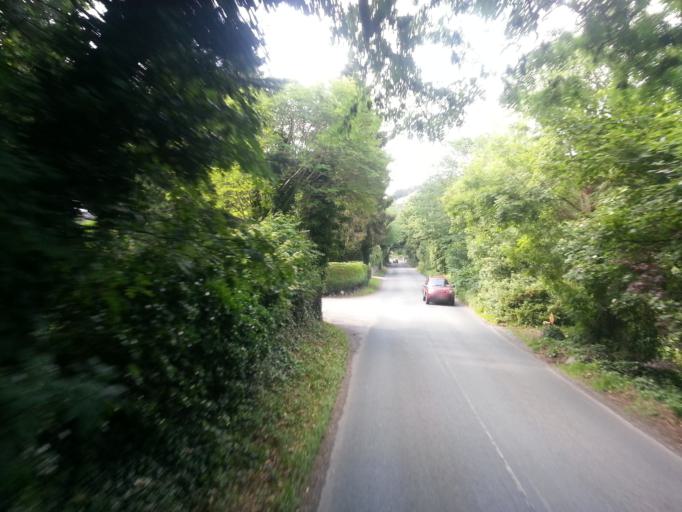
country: IE
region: Leinster
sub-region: Wicklow
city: Enniskerry
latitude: 53.2118
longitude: -6.1759
